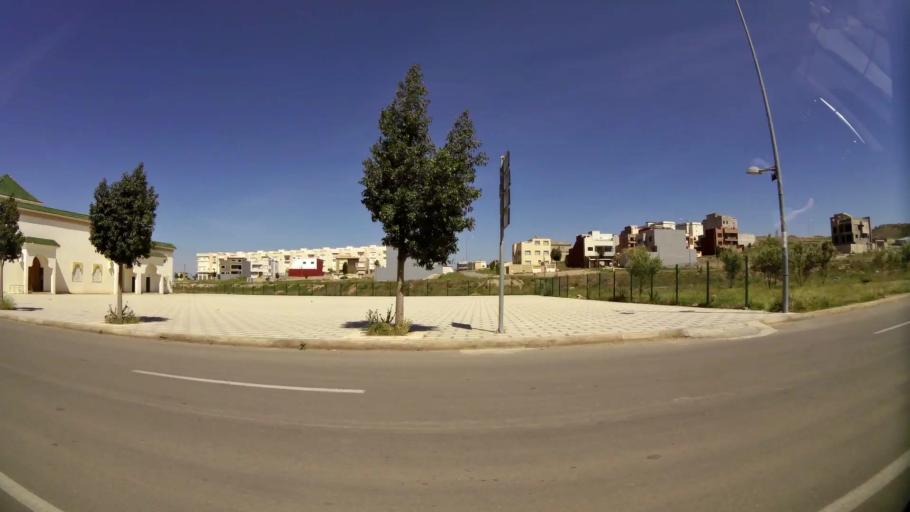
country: MA
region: Oriental
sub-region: Oujda-Angad
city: Oujda
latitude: 34.6533
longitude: -1.9135
